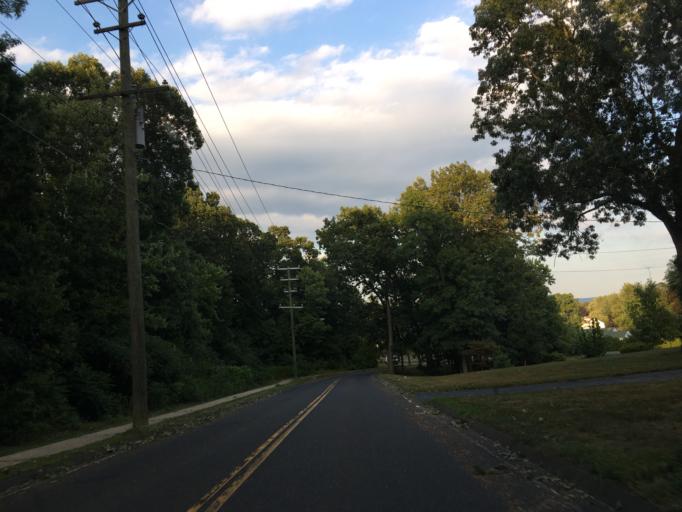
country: US
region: Connecticut
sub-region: Hartford County
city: Windsor Locks
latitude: 41.9195
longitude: -72.6365
